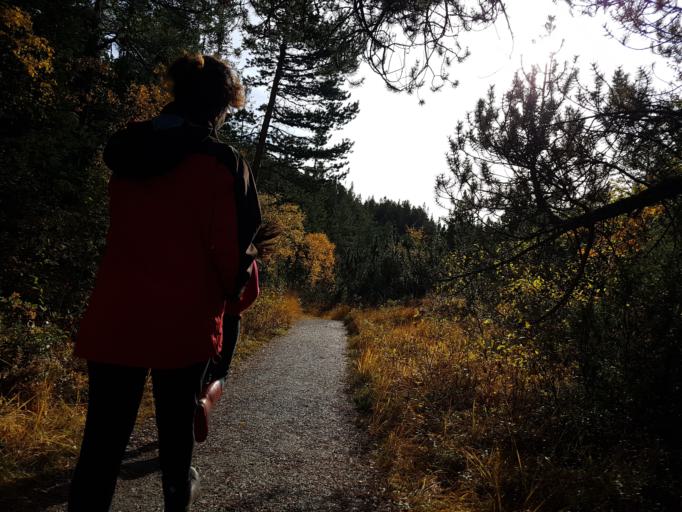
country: NO
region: Sor-Trondelag
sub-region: Trondheim
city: Trondheim
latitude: 63.4272
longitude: 10.2824
